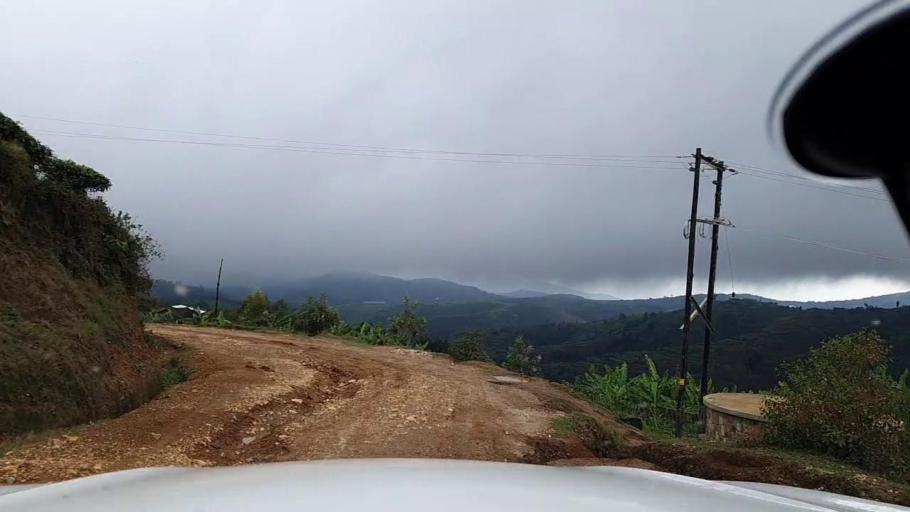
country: RW
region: Western Province
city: Kibuye
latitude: -2.0824
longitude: 29.5062
